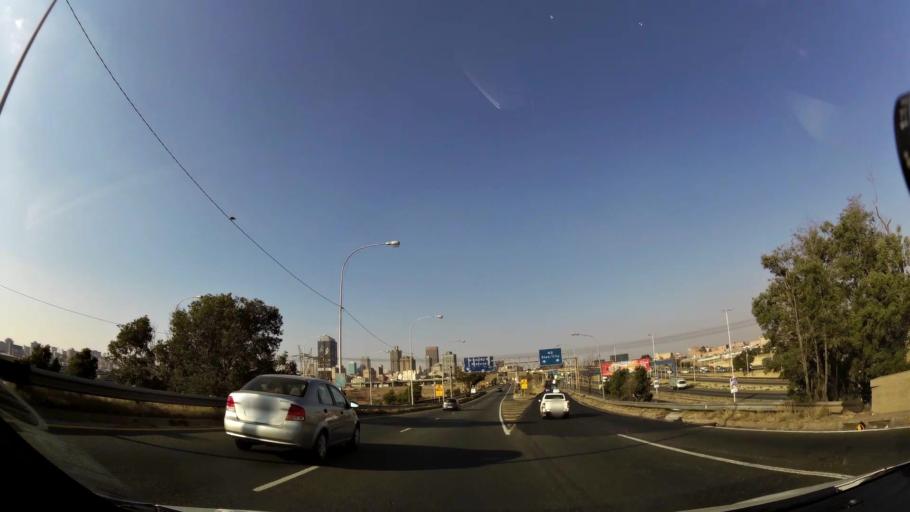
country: ZA
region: Gauteng
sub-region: City of Johannesburg Metropolitan Municipality
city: Johannesburg
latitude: -26.2113
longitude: 28.0261
